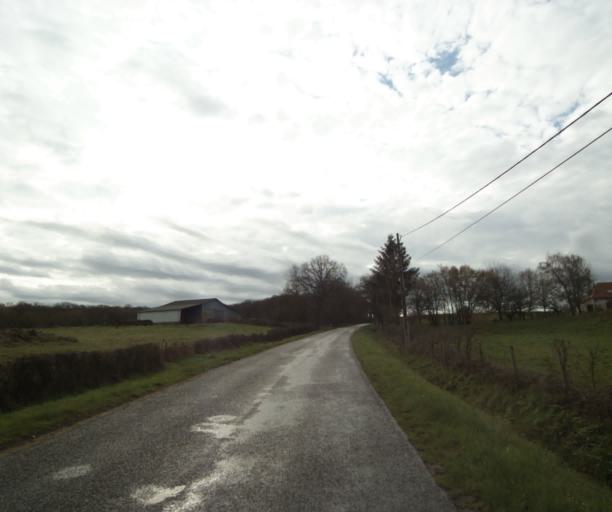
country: FR
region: Auvergne
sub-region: Departement de l'Allier
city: Toulon-sur-Allier
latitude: 46.5237
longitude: 3.4166
